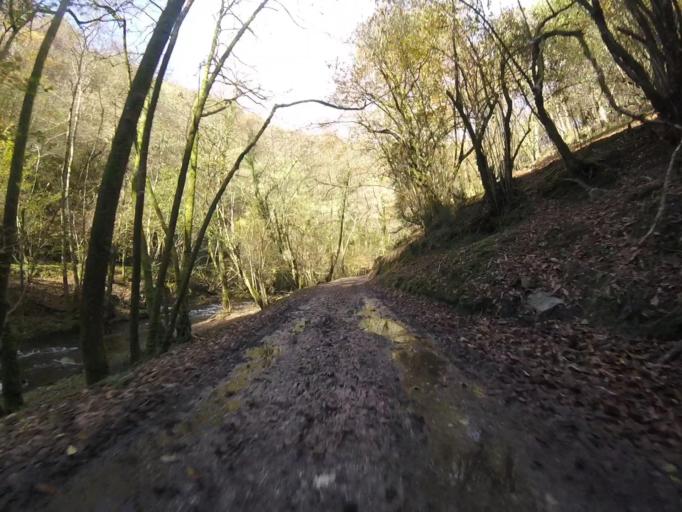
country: ES
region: Navarre
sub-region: Provincia de Navarra
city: Goizueta
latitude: 43.2128
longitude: -1.8042
